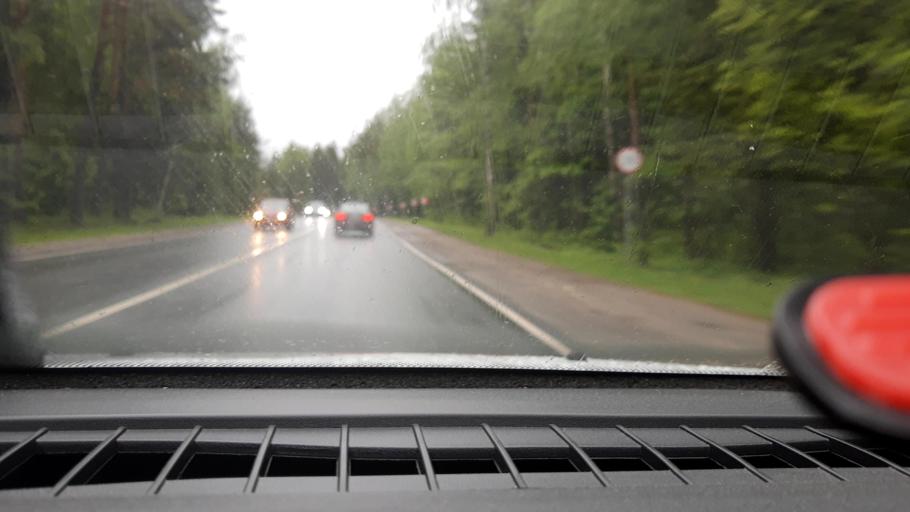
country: RU
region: Nizjnij Novgorod
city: Semenov
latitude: 56.7445
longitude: 44.3530
